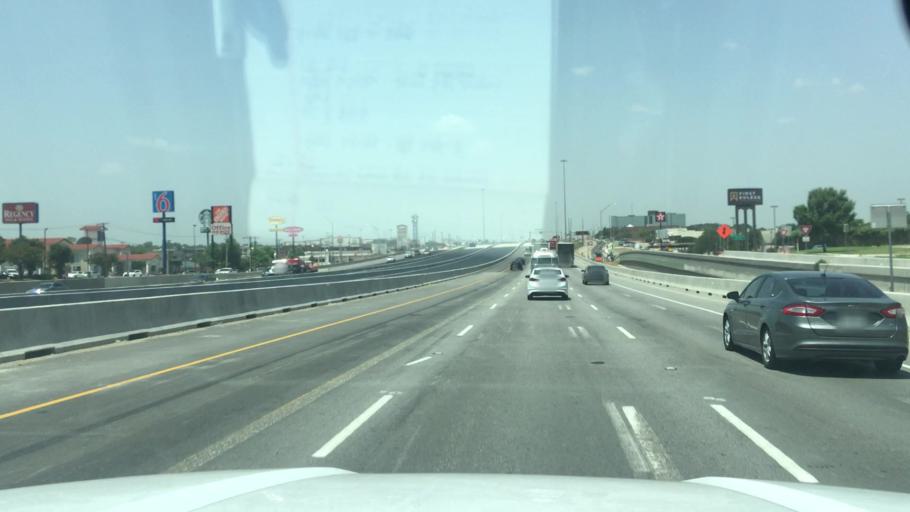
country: US
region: Texas
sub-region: Tarrant County
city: Euless
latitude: 32.8378
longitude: -97.0957
